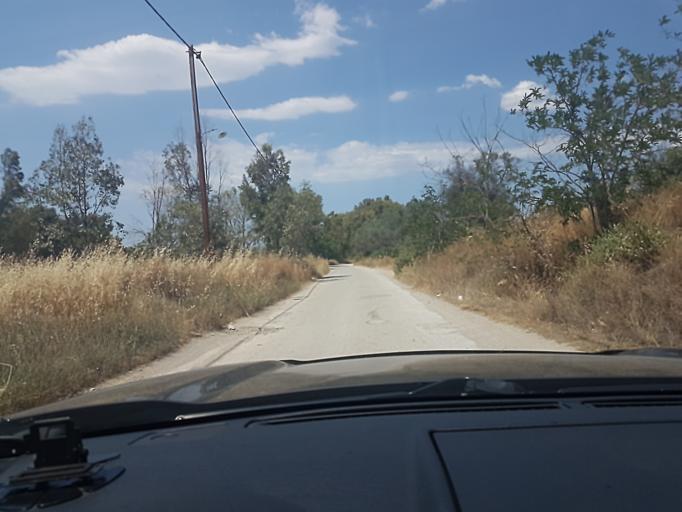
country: GR
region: Central Greece
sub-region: Nomos Evvoias
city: Vasilikon
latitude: 38.4188
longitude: 23.6617
